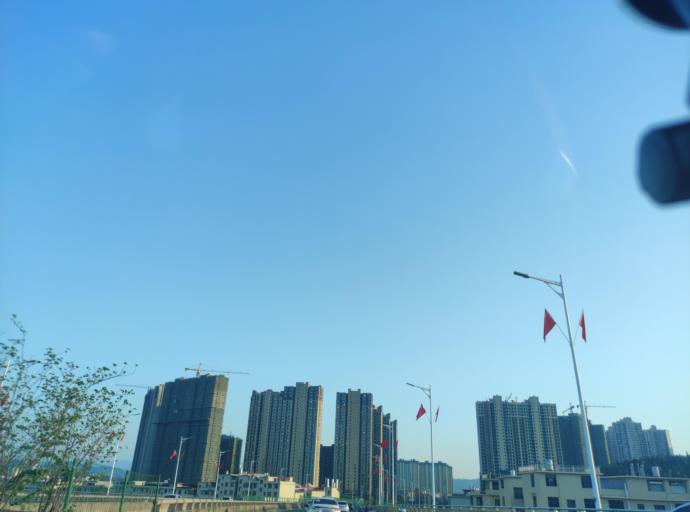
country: CN
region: Jiangxi Sheng
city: Pingxiang
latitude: 27.6400
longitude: 113.8291
